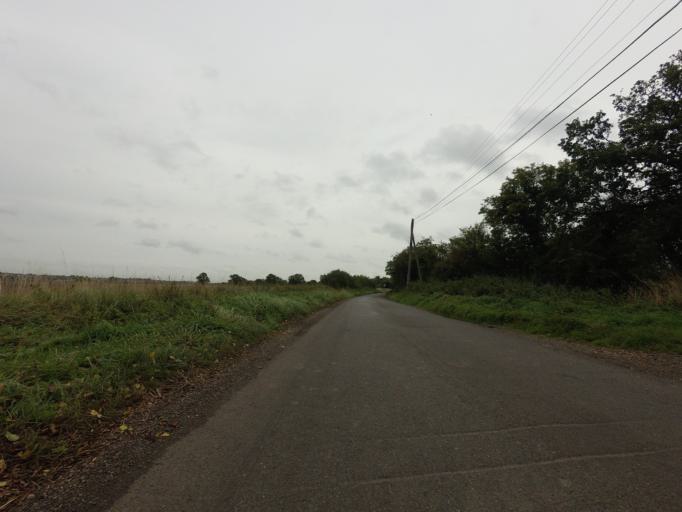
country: GB
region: England
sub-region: Hertfordshire
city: Buntingford
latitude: 51.9724
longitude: 0.0835
